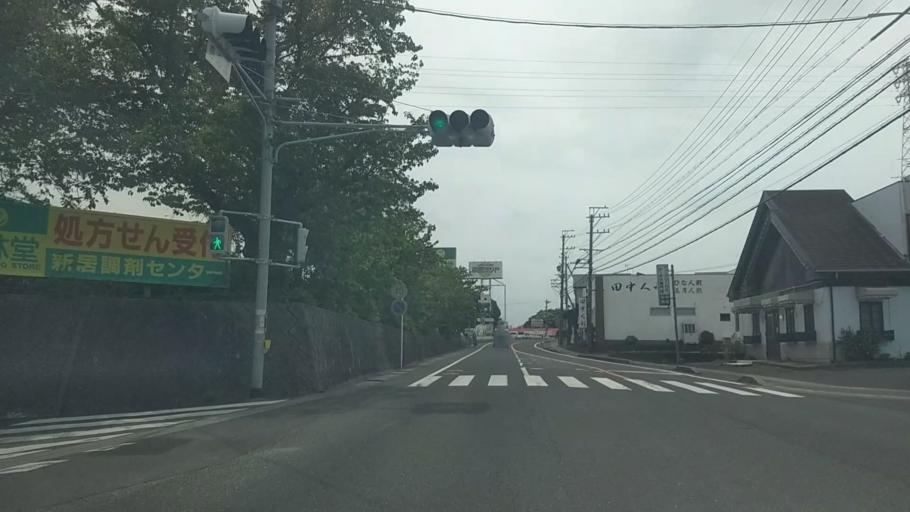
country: JP
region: Shizuoka
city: Kosai-shi
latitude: 34.7084
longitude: 137.5494
